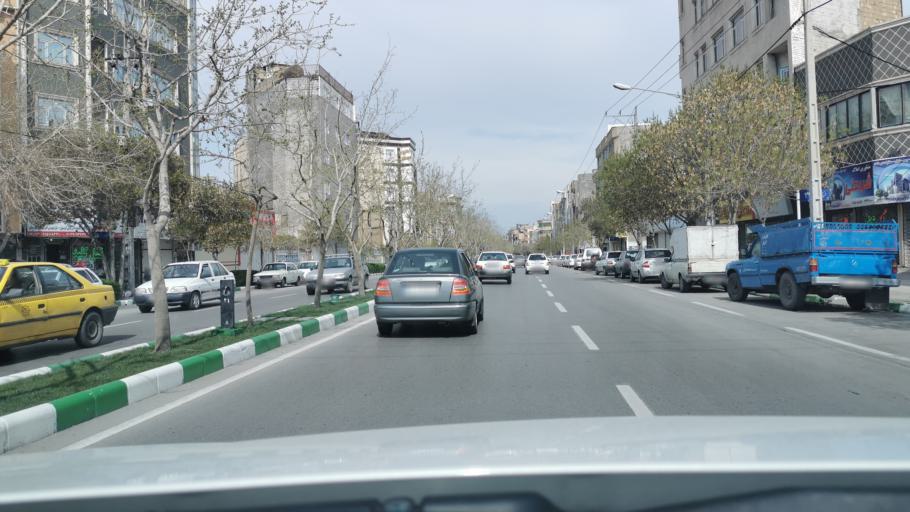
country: IR
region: Razavi Khorasan
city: Mashhad
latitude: 36.3164
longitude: 59.5976
